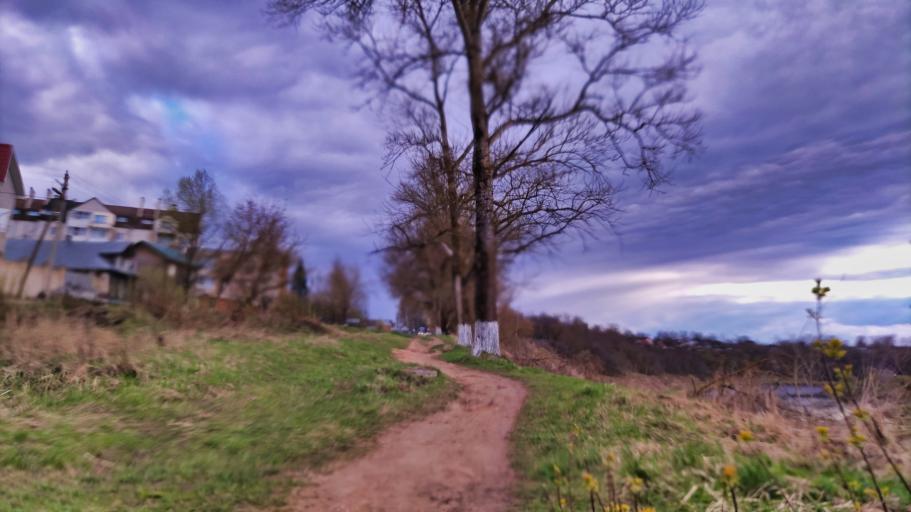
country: RU
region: Tverskaya
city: Rzhev
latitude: 56.2544
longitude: 34.3148
